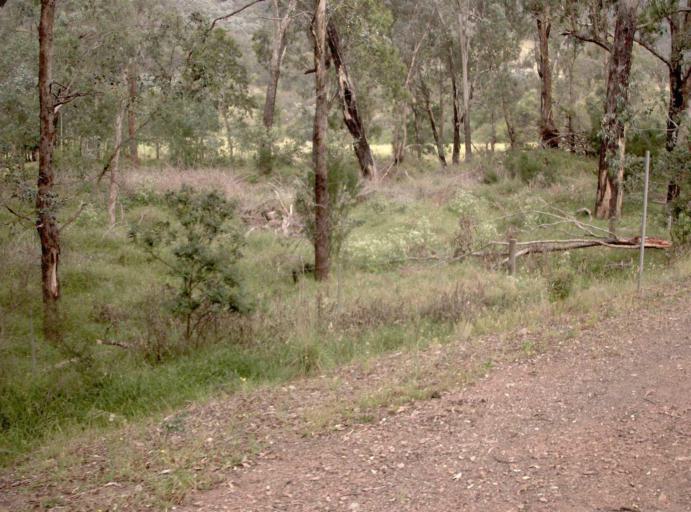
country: AU
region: Victoria
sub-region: Wellington
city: Heyfield
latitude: -37.7466
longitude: 146.6668
